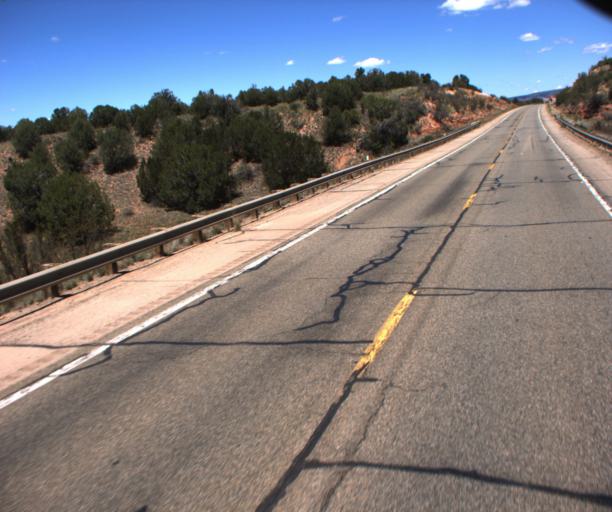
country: US
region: Arizona
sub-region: Yavapai County
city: Paulden
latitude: 34.9793
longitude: -112.4021
